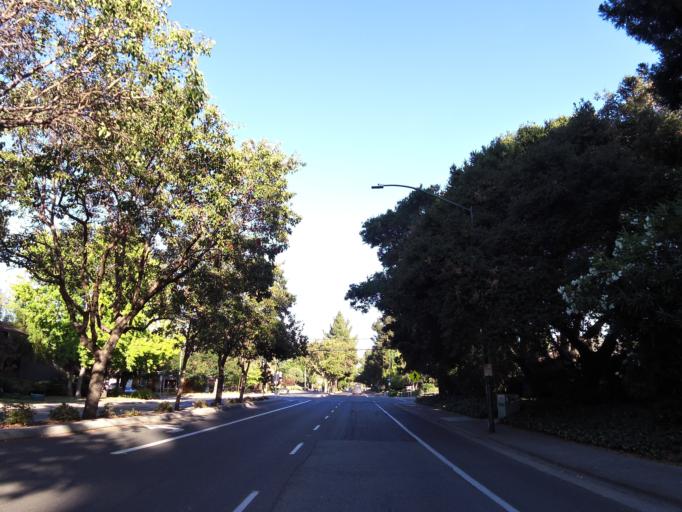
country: US
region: California
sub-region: Santa Clara County
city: Mountain View
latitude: 37.3986
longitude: -122.0657
